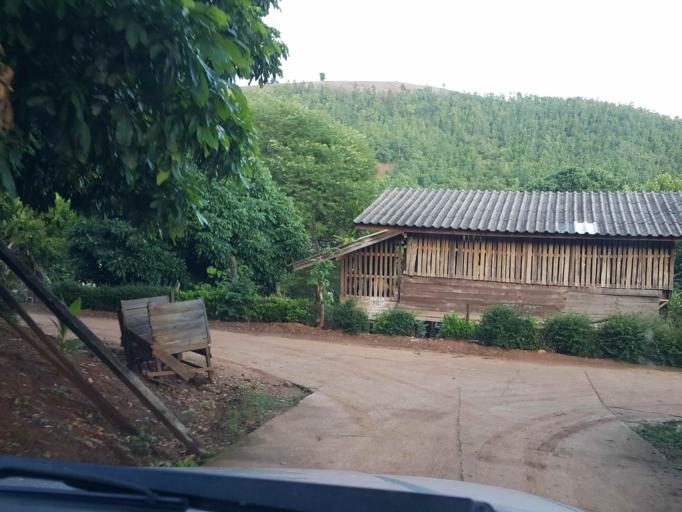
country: TH
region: Chiang Mai
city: Mae Chaem
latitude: 18.4970
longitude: 98.3970
